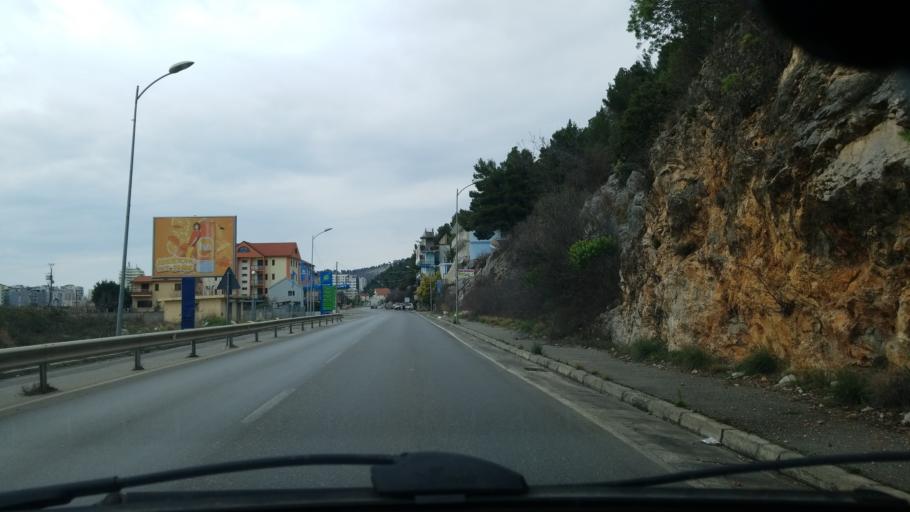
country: AL
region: Lezhe
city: Shengjin
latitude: 41.8059
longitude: 19.6103
